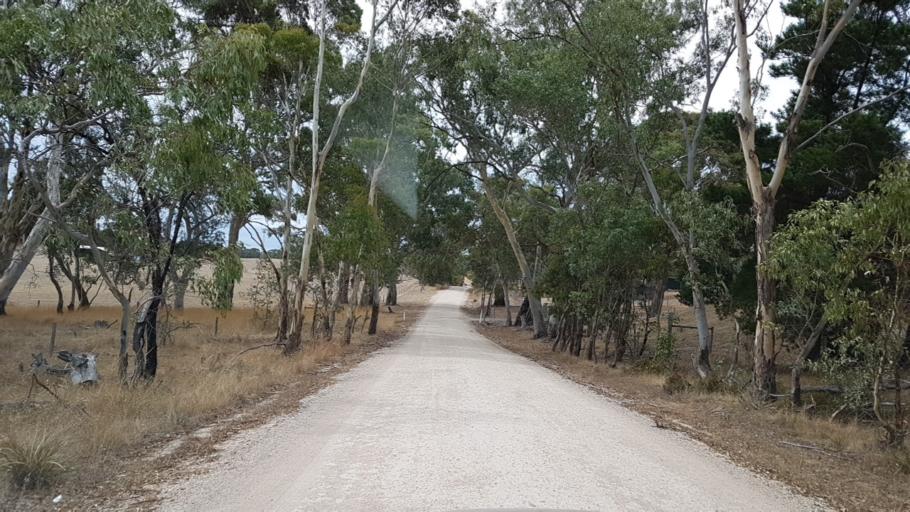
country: AU
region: South Australia
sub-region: Adelaide Hills
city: Birdwood
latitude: -34.7791
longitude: 138.9881
